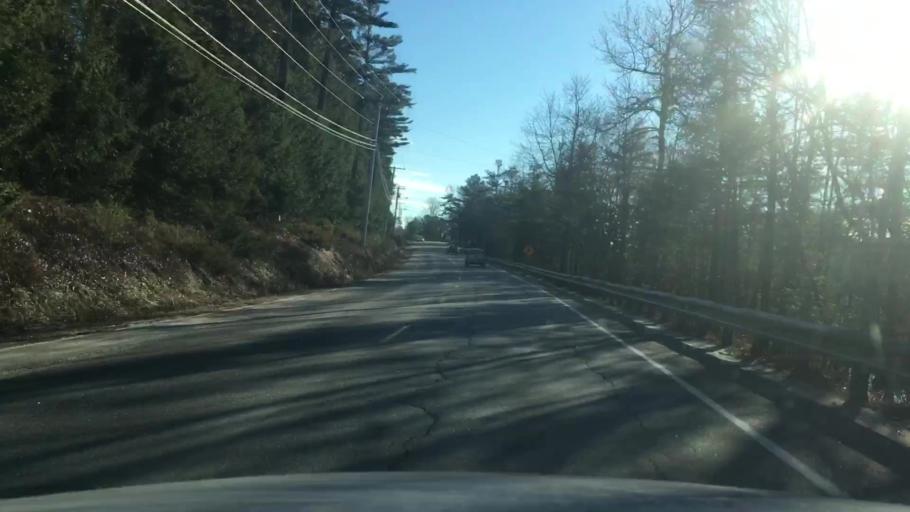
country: US
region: Maine
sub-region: Cumberland County
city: Brunswick
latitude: 43.8680
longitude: -69.9140
